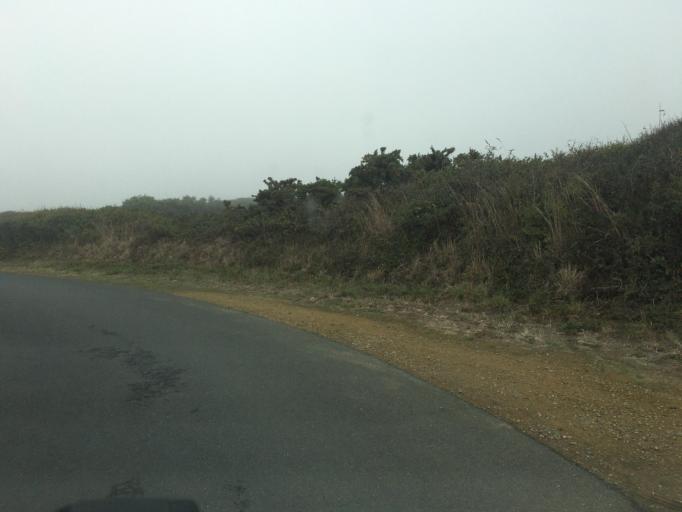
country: FR
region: Brittany
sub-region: Departement du Finistere
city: Plogoff
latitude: 48.0592
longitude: -4.7064
